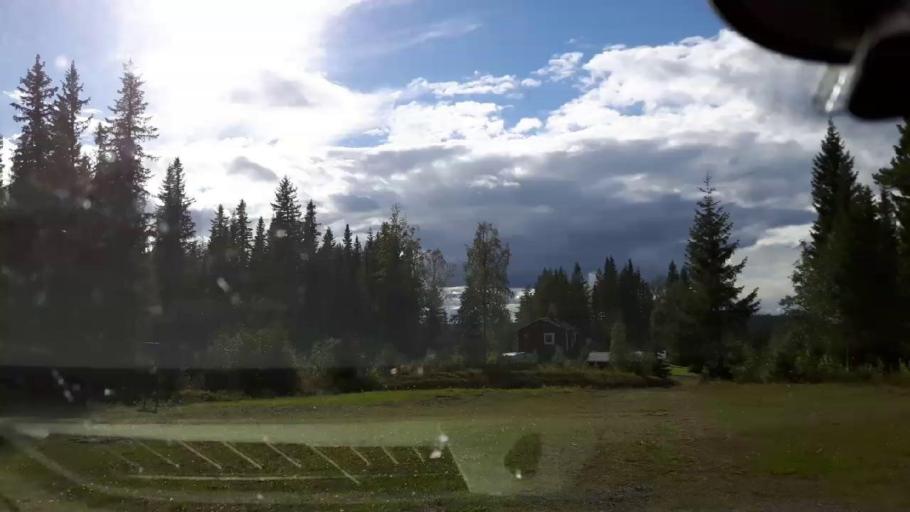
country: SE
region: Jaemtland
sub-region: Ragunda Kommun
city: Hammarstrand
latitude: 63.4422
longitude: 15.9574
